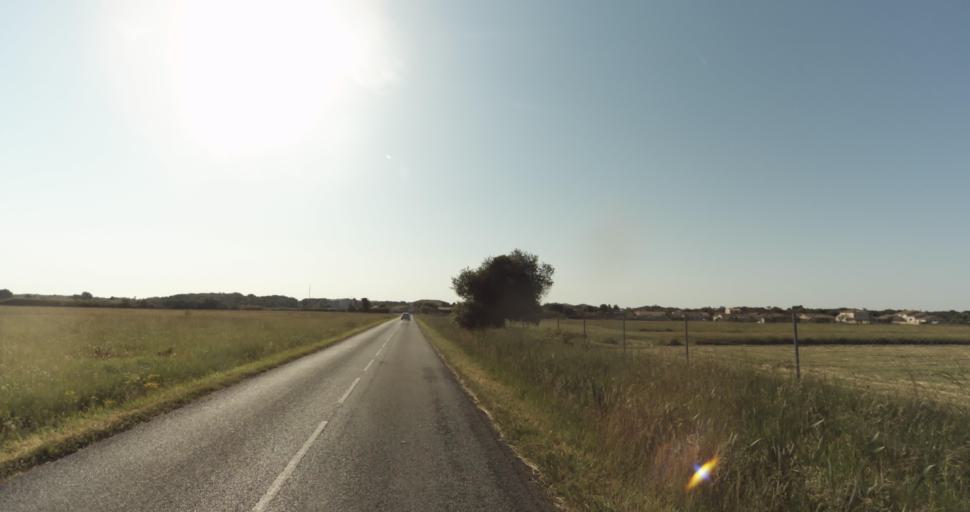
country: FR
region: Midi-Pyrenees
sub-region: Departement de la Haute-Garonne
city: Leguevin
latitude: 43.5752
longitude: 1.2398
